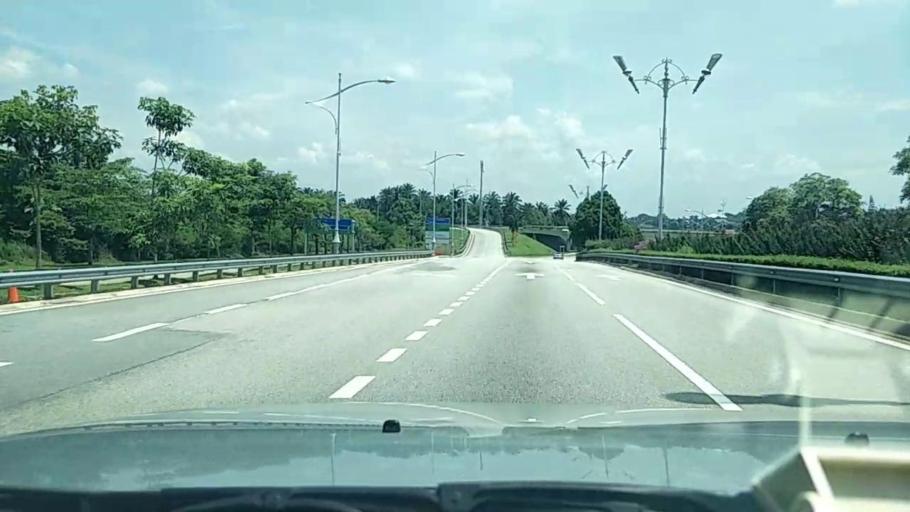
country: MY
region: Putrajaya
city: Putrajaya
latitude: 2.9555
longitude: 101.7019
